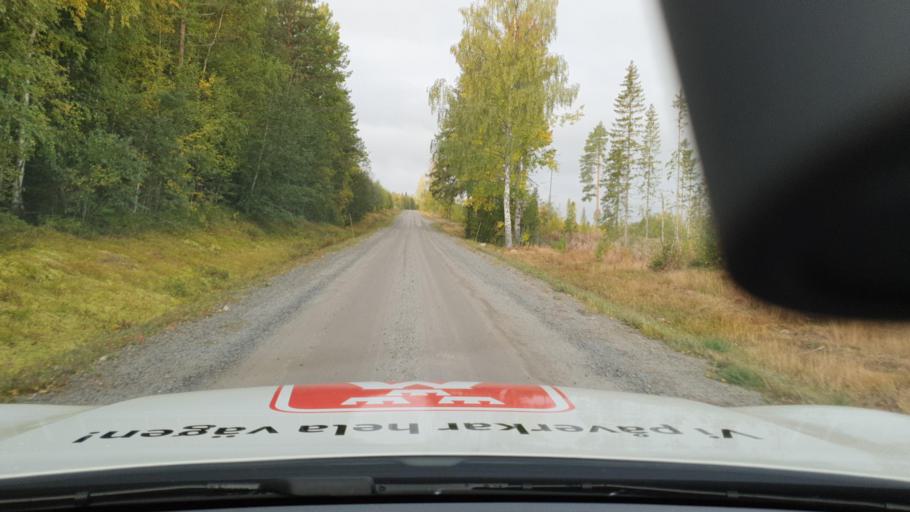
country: SE
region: Vaesterbotten
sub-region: Lycksele Kommun
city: Lycksele
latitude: 64.2098
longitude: 18.7624
